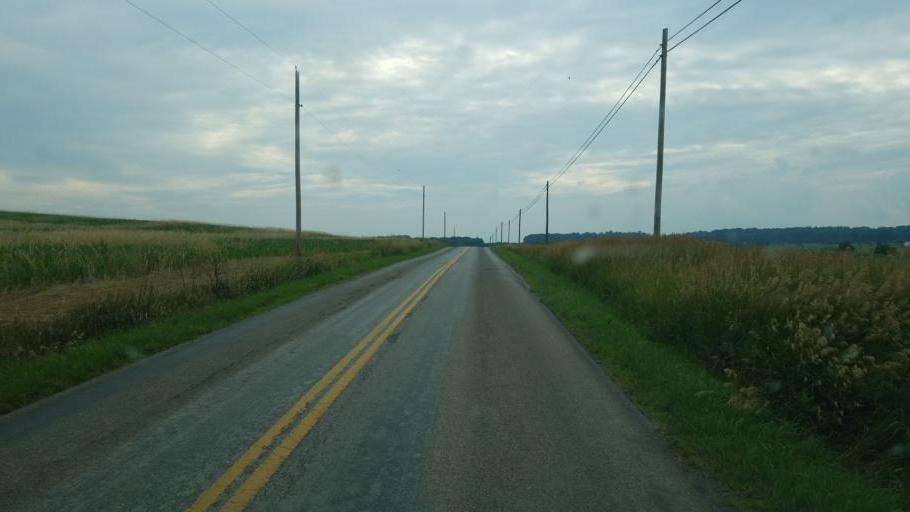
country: US
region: Ohio
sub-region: Wayne County
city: Apple Creek
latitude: 40.7557
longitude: -81.8084
